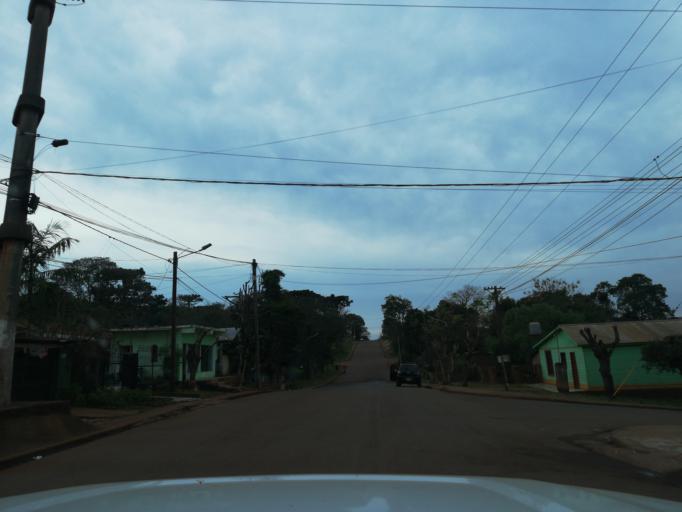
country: AR
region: Misiones
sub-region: Departamento de San Pedro
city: San Pedro
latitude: -26.6225
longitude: -54.1057
